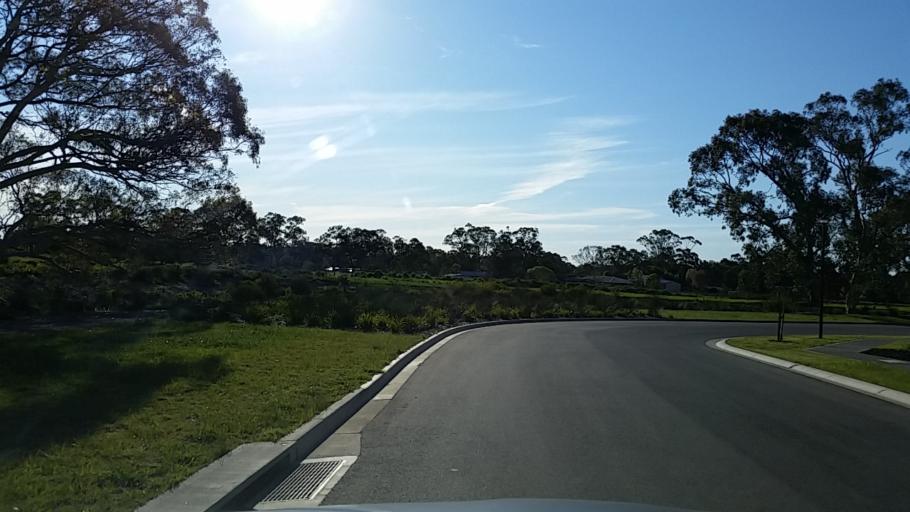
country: AU
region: South Australia
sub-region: Mount Barker
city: Meadows
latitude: -35.1850
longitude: 138.7587
